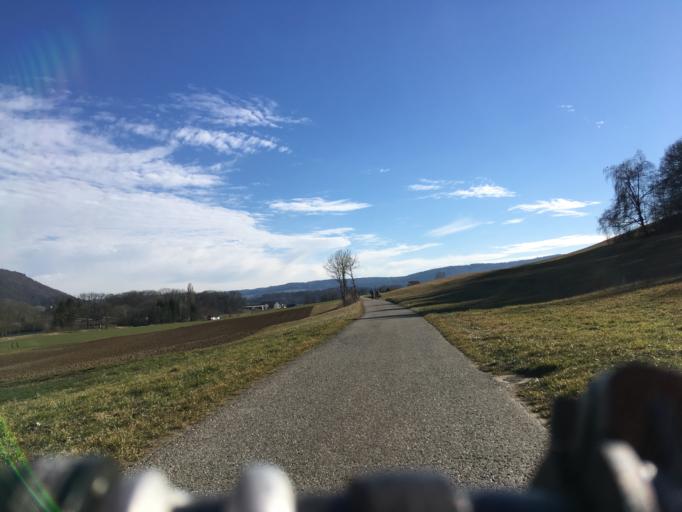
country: CH
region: Schaffhausen
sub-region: Bezirk Stein
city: Ramsen
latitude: 47.6939
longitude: 8.8115
